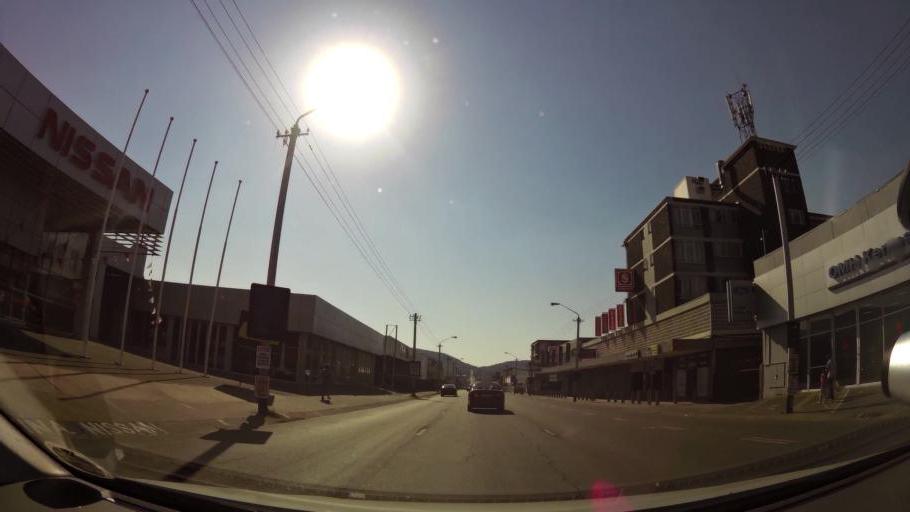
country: ZA
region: Gauteng
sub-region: City of Tshwane Metropolitan Municipality
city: Pretoria
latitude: -25.7138
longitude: 28.2017
